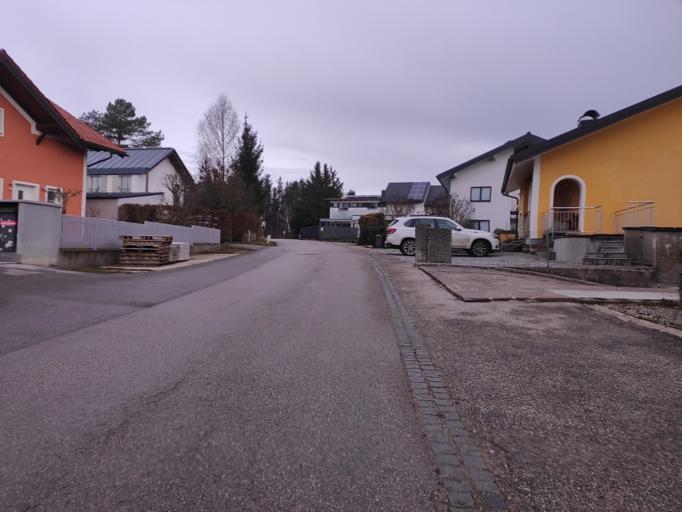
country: AT
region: Salzburg
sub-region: Politischer Bezirk Salzburg-Umgebung
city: Elixhausen
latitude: 47.8957
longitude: 13.0573
